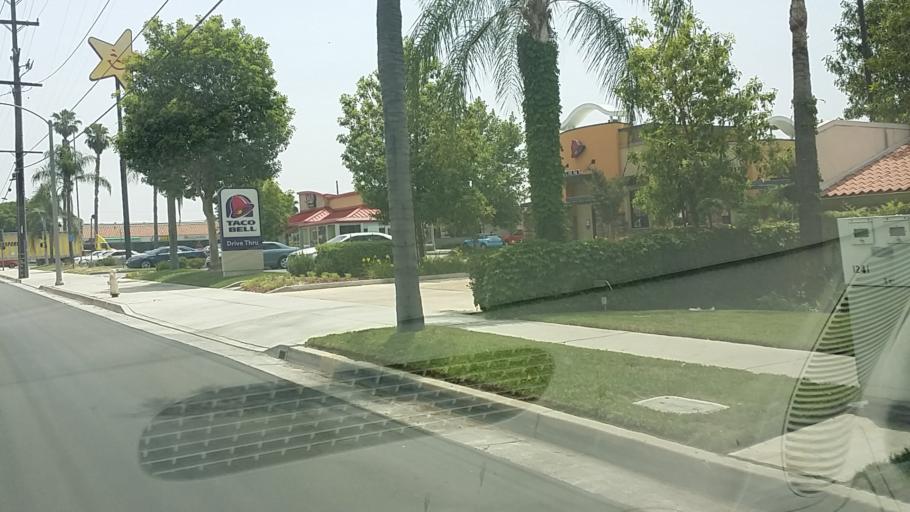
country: US
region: California
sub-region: San Bernardino County
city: Redlands
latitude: 34.0628
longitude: -117.2014
